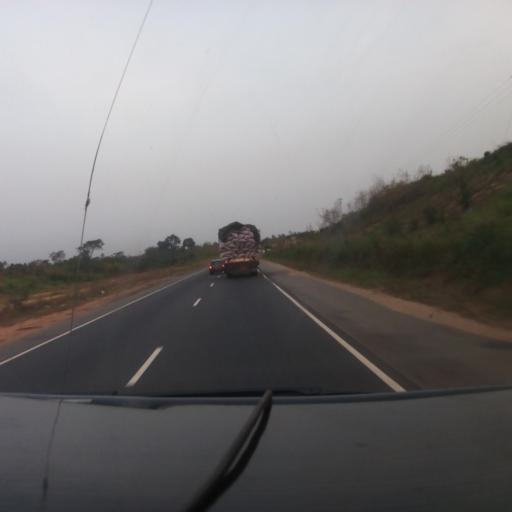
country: GH
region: Eastern
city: Nsawam
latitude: 5.8875
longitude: -0.3793
